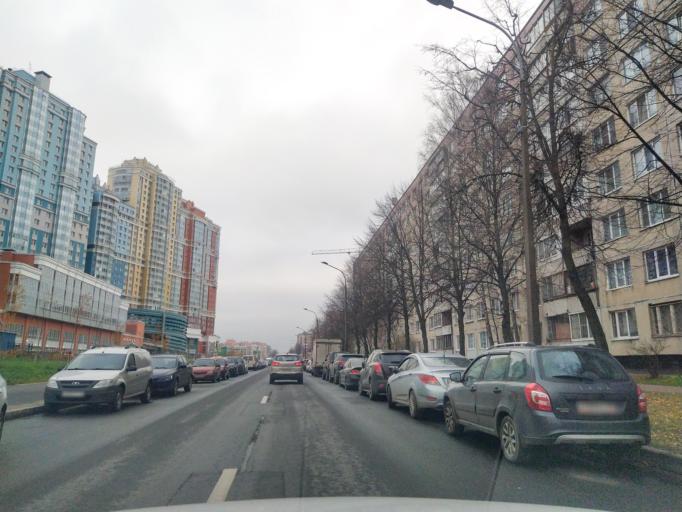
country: RU
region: St.-Petersburg
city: Sosnovka
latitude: 60.0430
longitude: 30.3638
